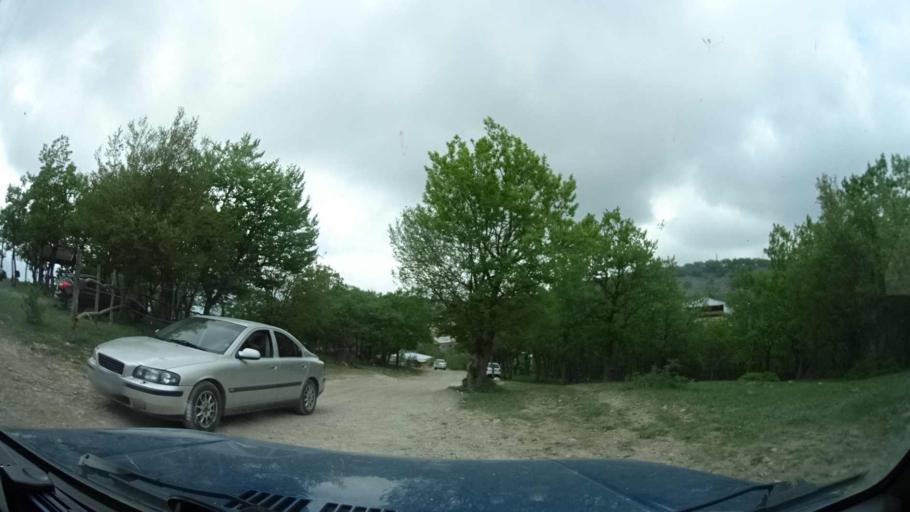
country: RU
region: Dagestan
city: Dubki
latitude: 43.0205
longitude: 46.8314
